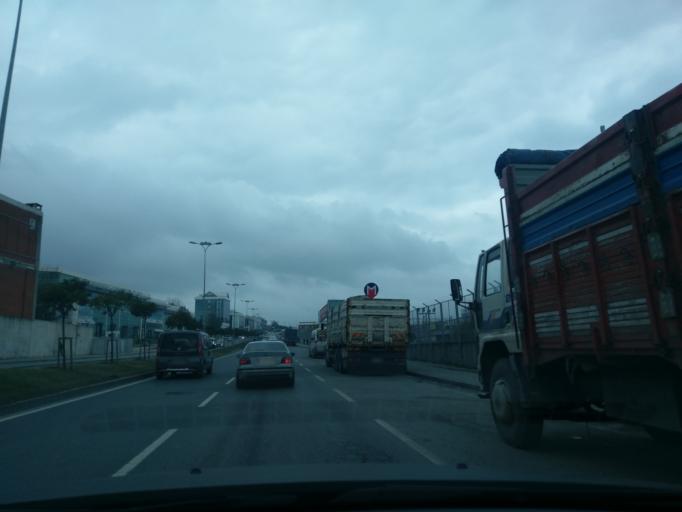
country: TR
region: Istanbul
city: Basaksehir
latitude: 41.0715
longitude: 28.8036
